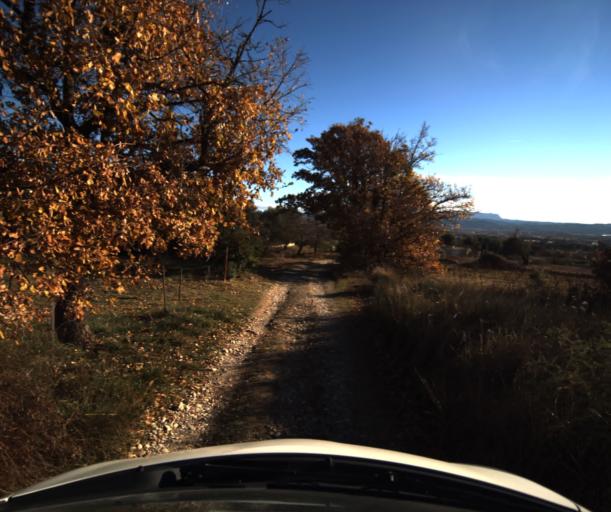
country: FR
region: Provence-Alpes-Cote d'Azur
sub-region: Departement du Vaucluse
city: Pertuis
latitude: 43.7069
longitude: 5.4779
